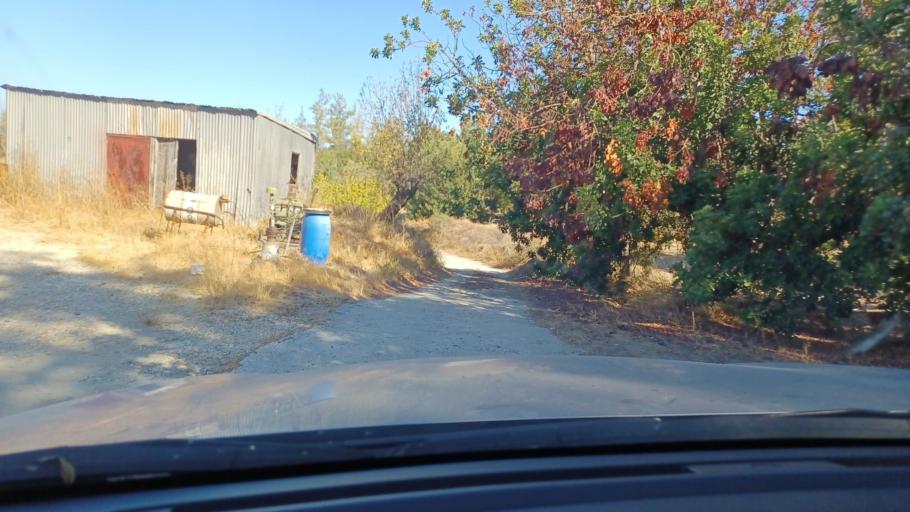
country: CY
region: Pafos
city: Polis
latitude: 35.0102
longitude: 32.5040
